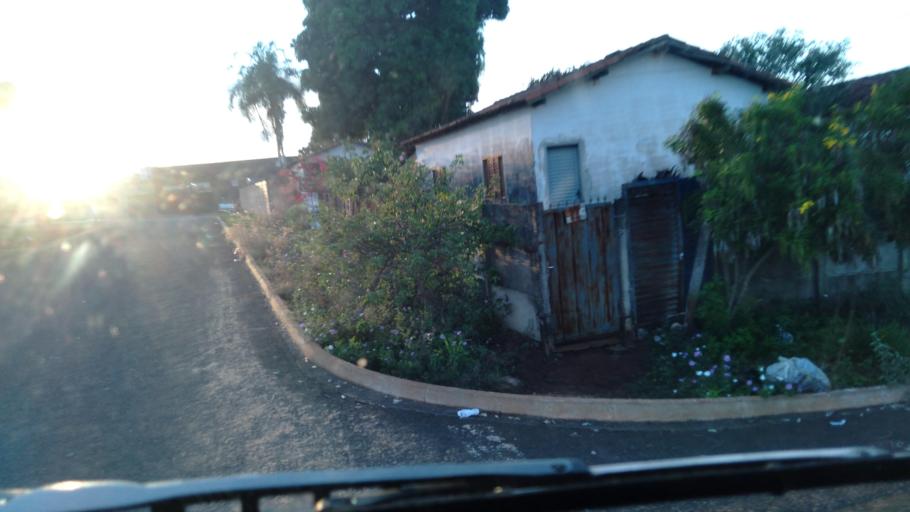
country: BR
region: Goias
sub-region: Mineiros
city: Mineiros
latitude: -17.5705
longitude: -52.5709
